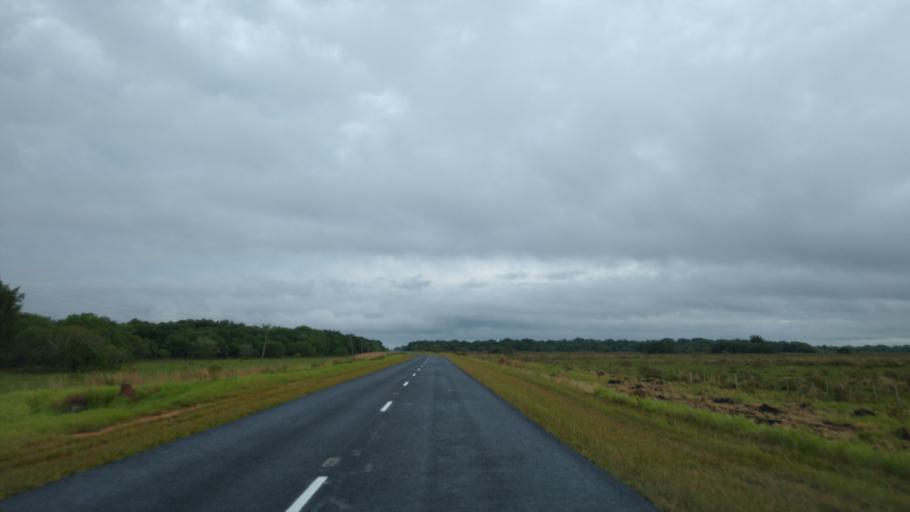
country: AR
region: Corrientes
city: Loreto
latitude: -27.7543
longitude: -57.2583
